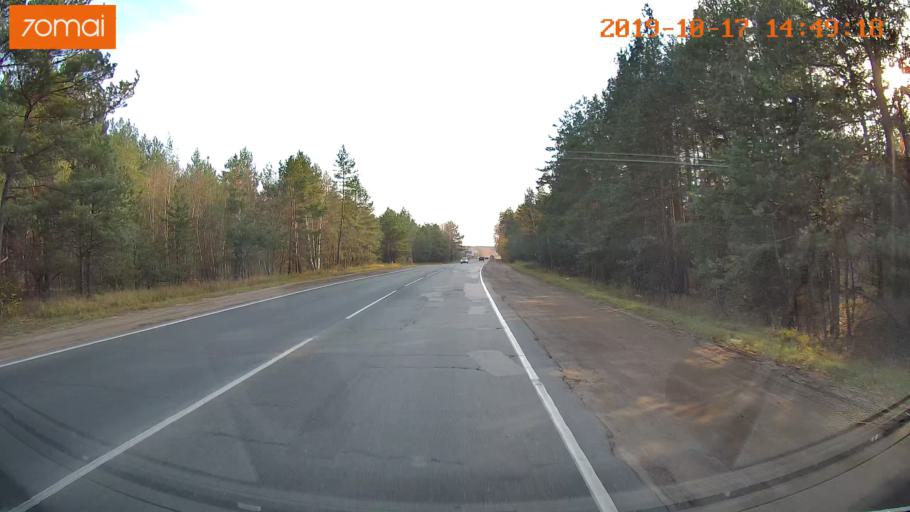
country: RU
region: Rjazan
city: Polyany
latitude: 54.7488
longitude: 39.8396
